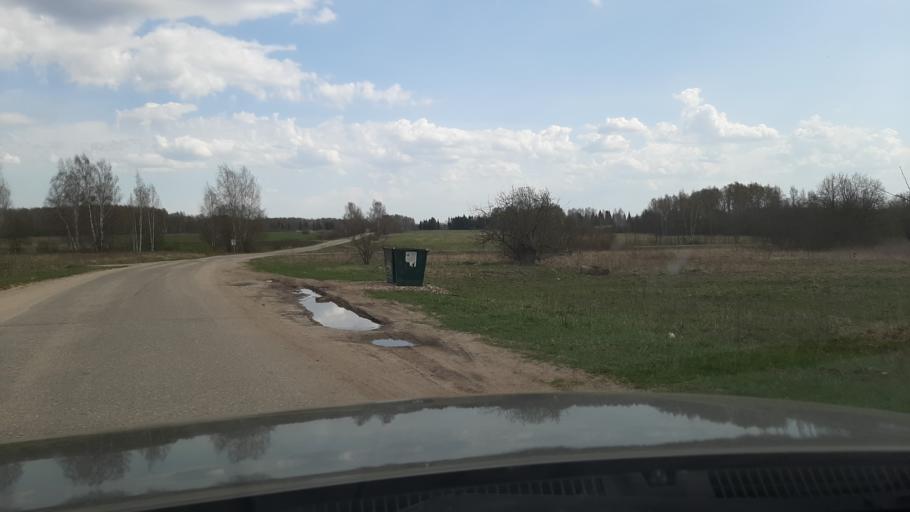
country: RU
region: Ivanovo
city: Furmanov
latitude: 57.2993
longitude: 41.1665
